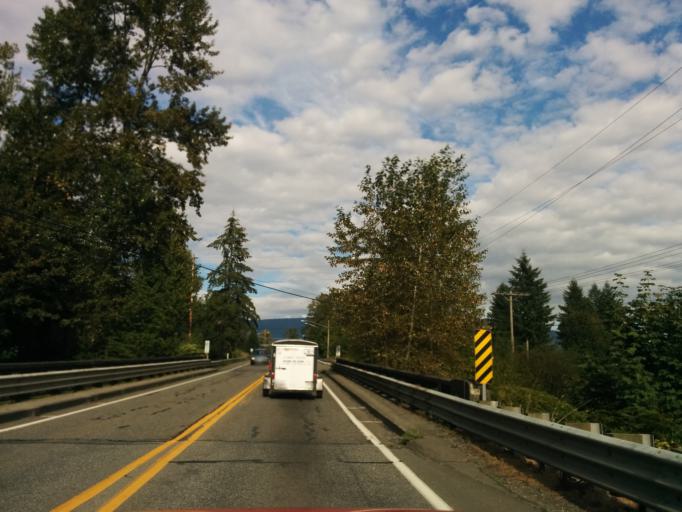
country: US
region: Washington
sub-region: Snohomish County
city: Sultan
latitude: 47.8640
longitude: -121.8008
